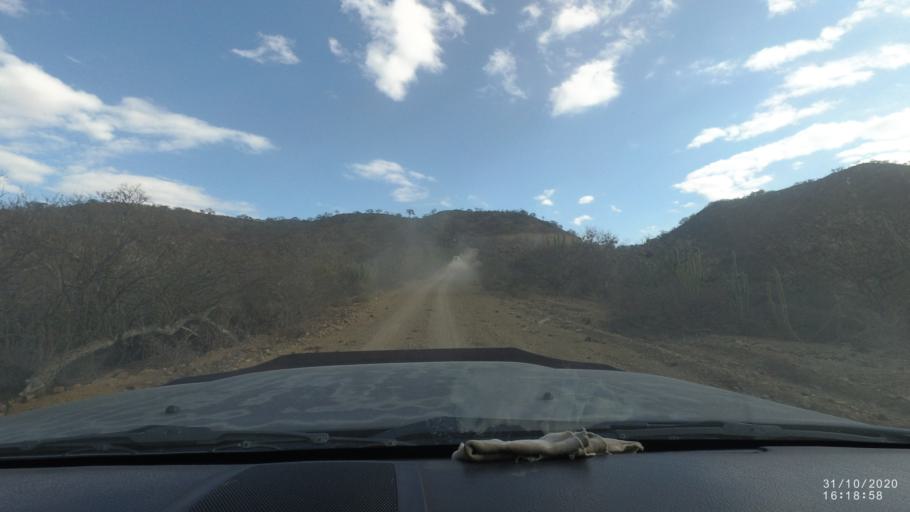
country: BO
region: Chuquisaca
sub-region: Provincia Zudanez
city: Mojocoya
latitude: -18.3933
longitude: -64.6031
